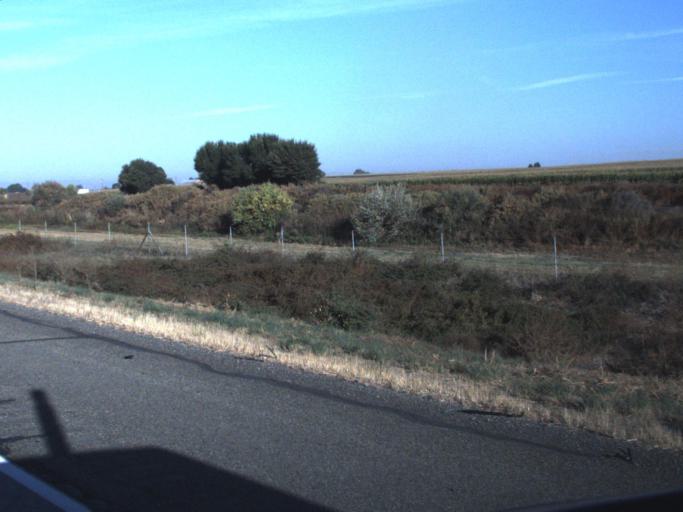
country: US
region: Washington
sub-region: Yakima County
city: Granger
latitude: 46.3387
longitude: -120.1594
